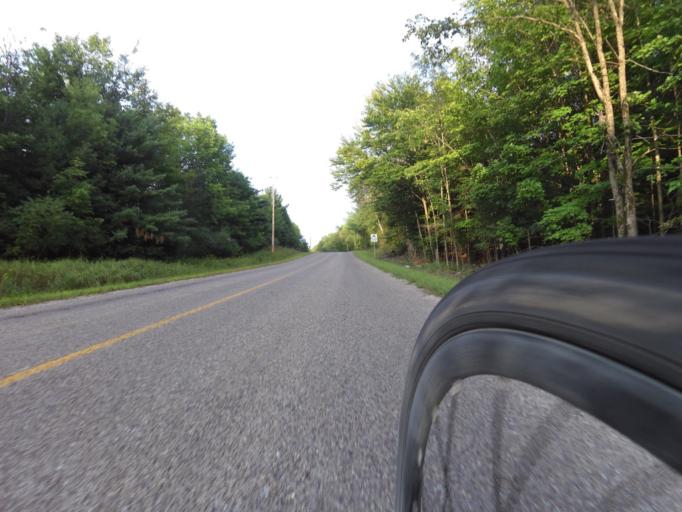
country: CA
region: Ontario
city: Gananoque
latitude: 44.5769
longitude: -76.3293
